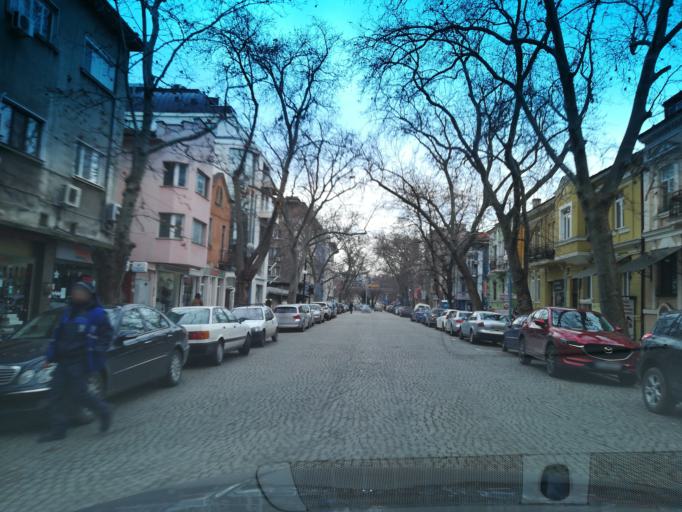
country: BG
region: Plovdiv
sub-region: Obshtina Plovdiv
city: Plovdiv
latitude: 42.1374
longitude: 24.7442
